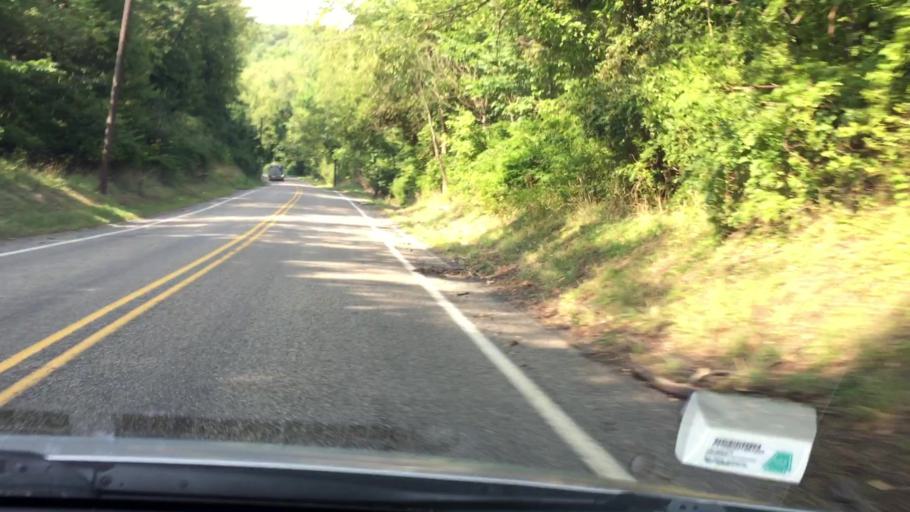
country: US
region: Pennsylvania
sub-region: Allegheny County
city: Franklin Park
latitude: 40.5802
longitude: -80.1191
